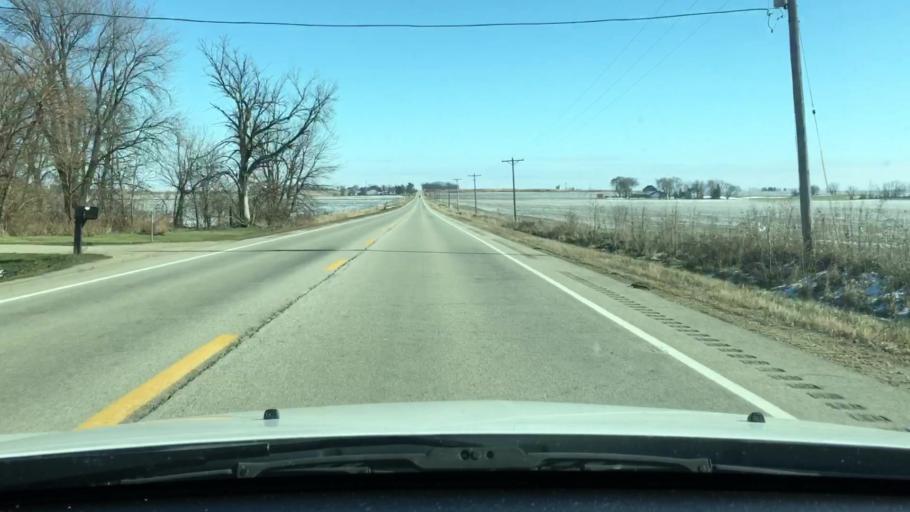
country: US
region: Illinois
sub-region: DeKalb County
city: Malta
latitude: 42.0008
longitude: -88.9266
